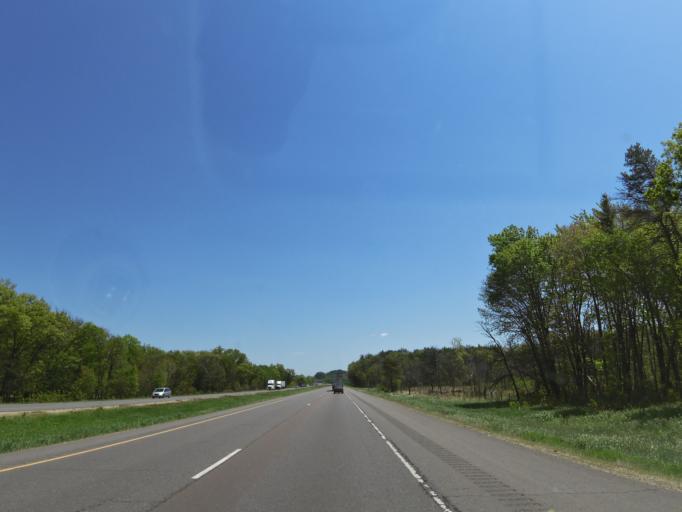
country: US
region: Wisconsin
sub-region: Juneau County
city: New Lisbon
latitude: 43.9324
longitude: -90.2876
